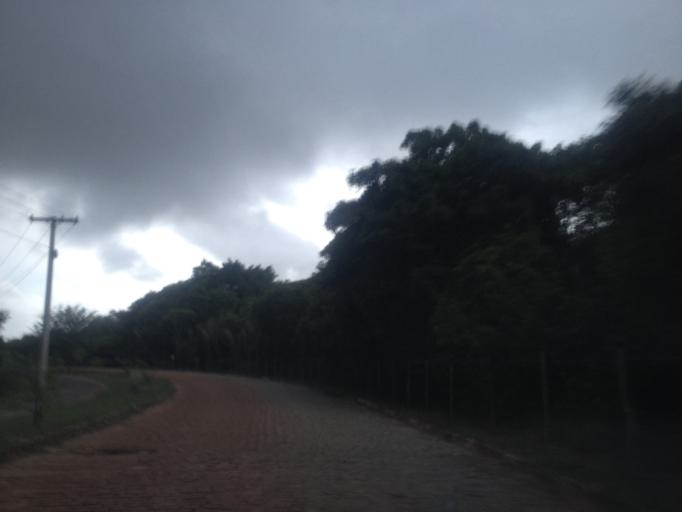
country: BR
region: Bahia
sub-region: Mata De Sao Joao
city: Mata de Sao Joao
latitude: -12.5676
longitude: -38.0210
